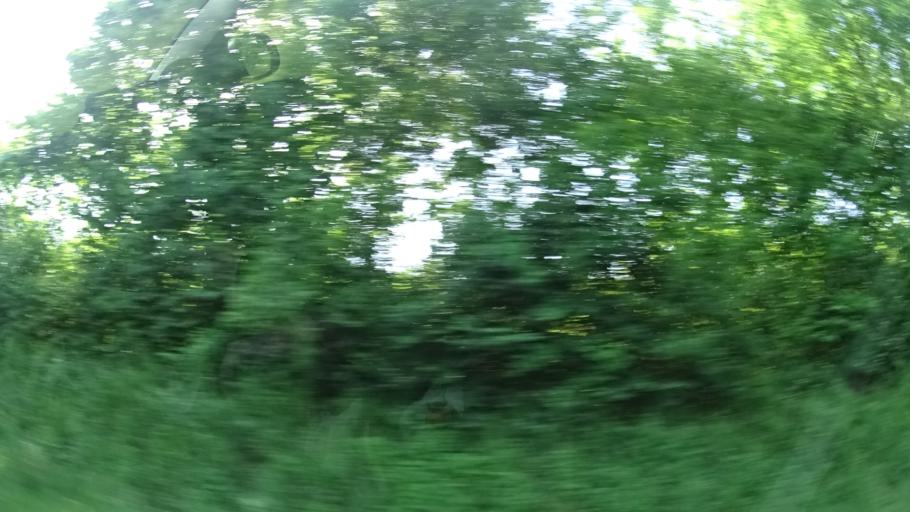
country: DE
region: Hesse
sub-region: Regierungsbezirk Giessen
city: Grossen Buseck
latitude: 50.6129
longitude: 8.8021
